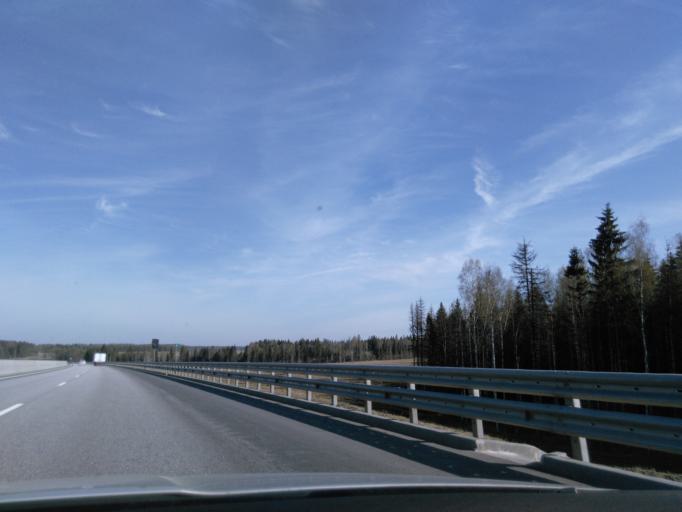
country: RU
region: Moskovskaya
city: Mendeleyevo
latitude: 56.0829
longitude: 37.2081
